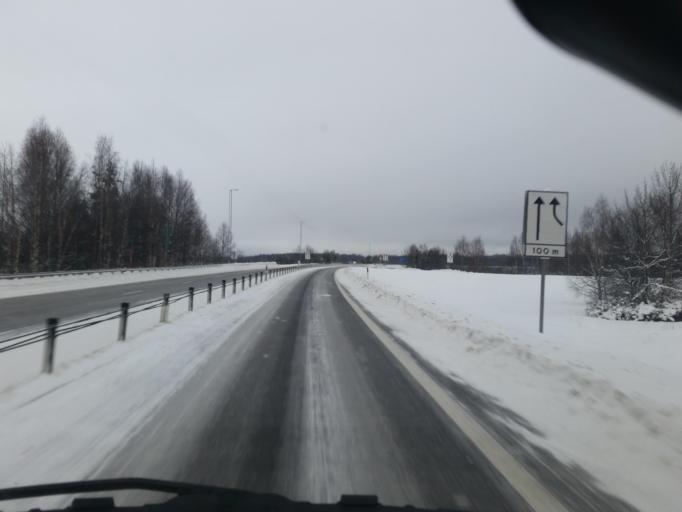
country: SE
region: Norrbotten
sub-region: Pitea Kommun
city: Bergsviken
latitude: 65.3092
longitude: 21.4079
